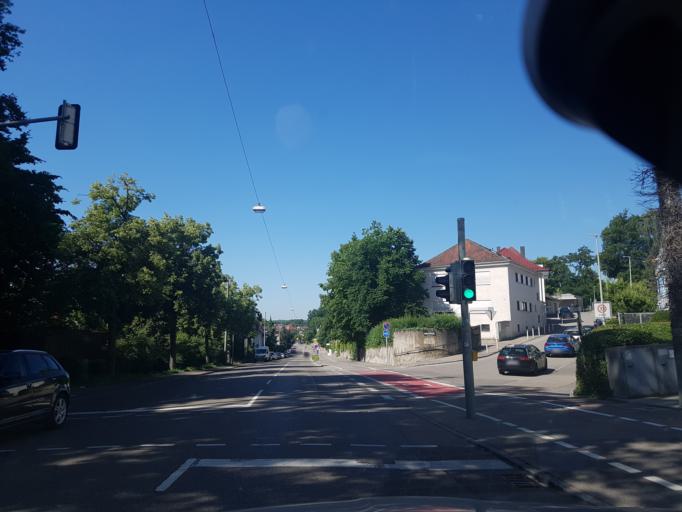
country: DE
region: Baden-Wuerttemberg
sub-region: Tuebingen Region
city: Ulm
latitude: 48.4110
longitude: 10.0049
